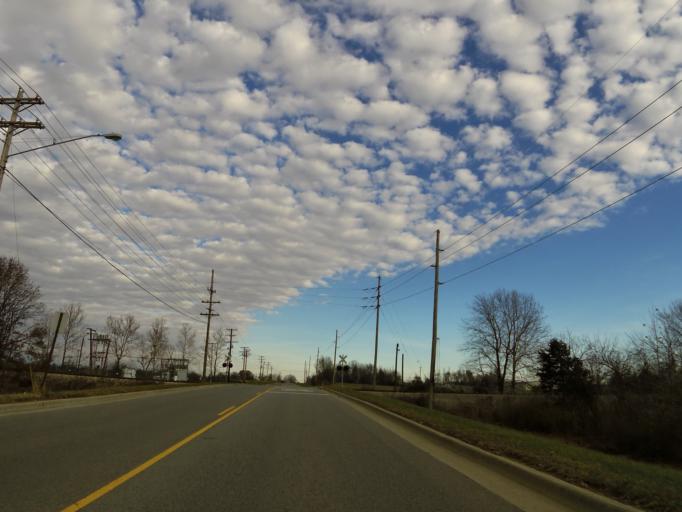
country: US
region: Illinois
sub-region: Jefferson County
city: Mount Vernon
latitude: 38.3276
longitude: -88.9700
